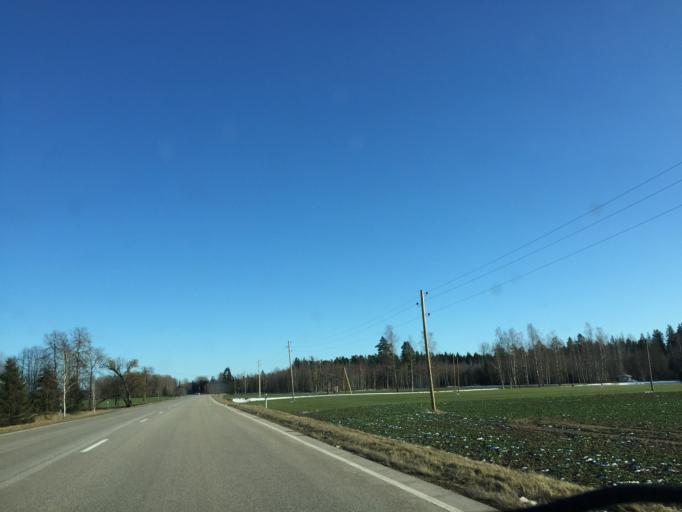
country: LV
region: Talsu Rajons
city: Stende
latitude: 57.2084
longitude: 22.5189
